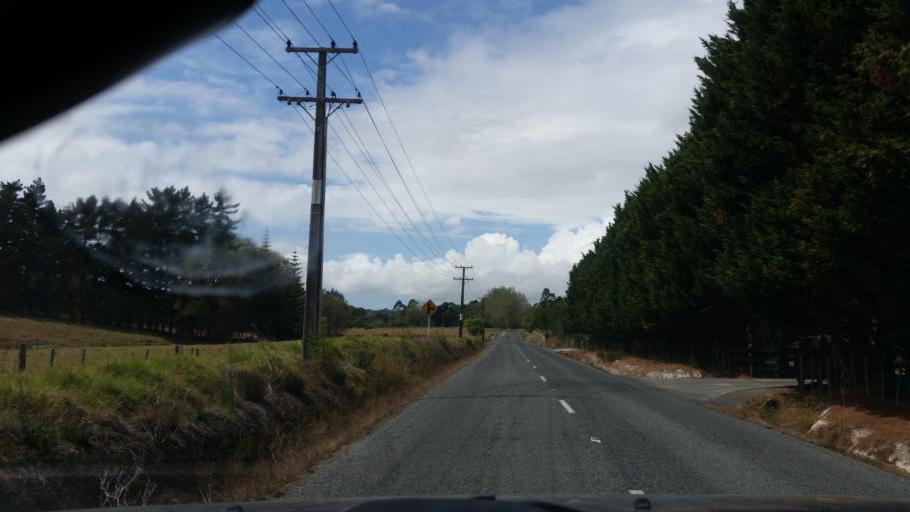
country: NZ
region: Auckland
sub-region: Auckland
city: Wellsford
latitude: -36.1203
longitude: 174.5505
